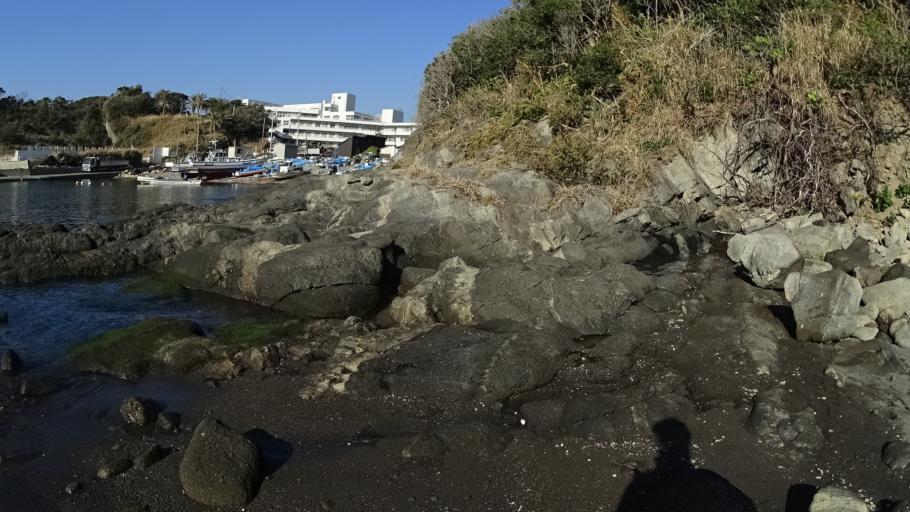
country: JP
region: Kanagawa
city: Miura
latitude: 35.1934
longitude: 139.6093
